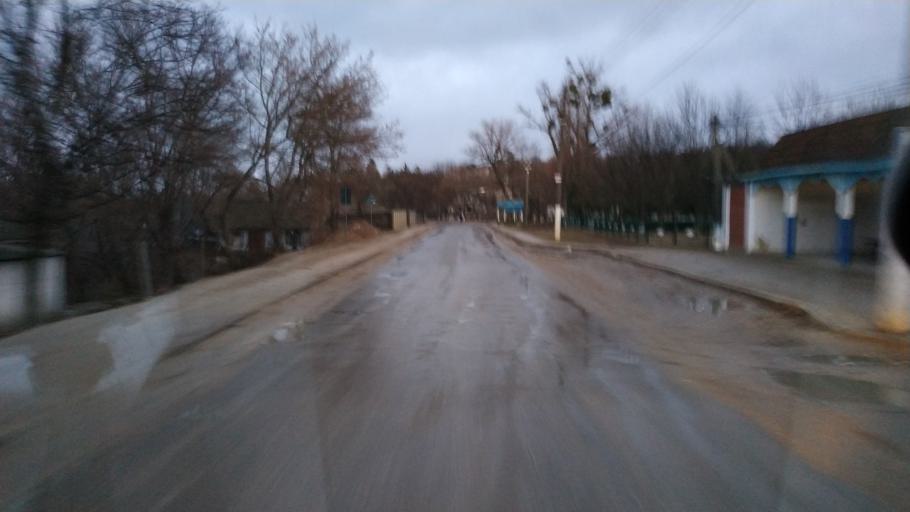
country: MD
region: Taraclia
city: Telenesti
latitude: 47.3731
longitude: 28.3685
